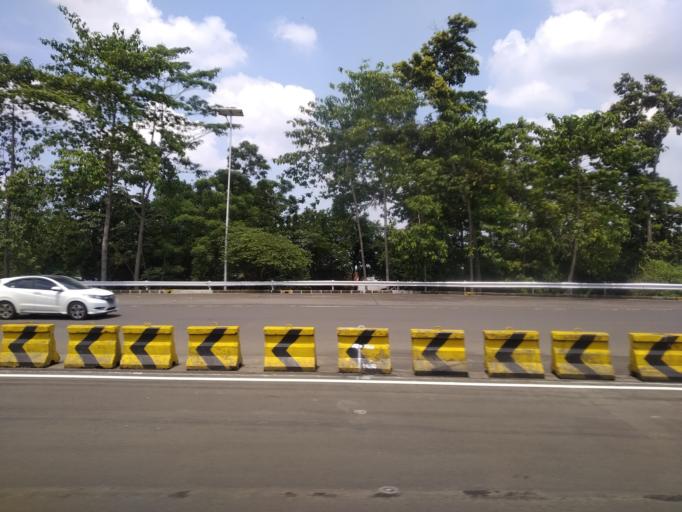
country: ID
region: West Java
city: Bogor
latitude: -6.5969
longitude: 106.8193
